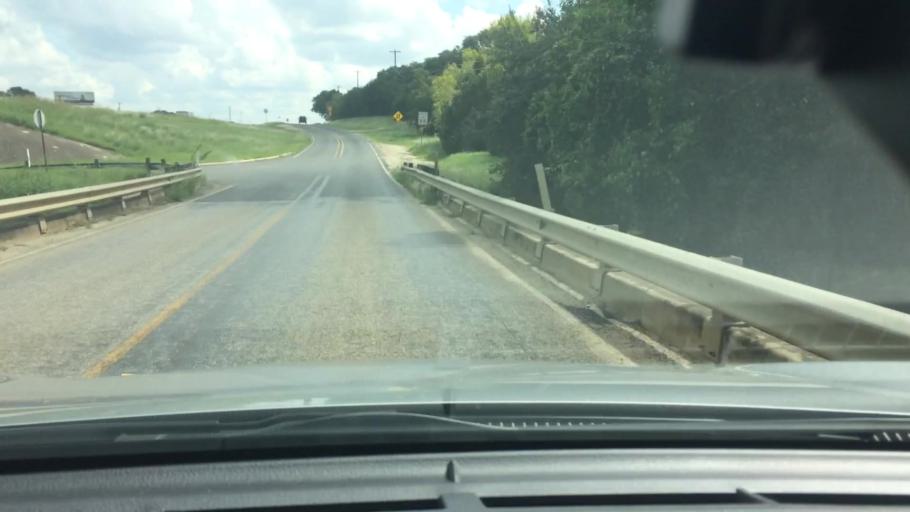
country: US
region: Texas
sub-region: Bexar County
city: Scenic Oaks
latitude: 29.7386
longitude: -98.6879
